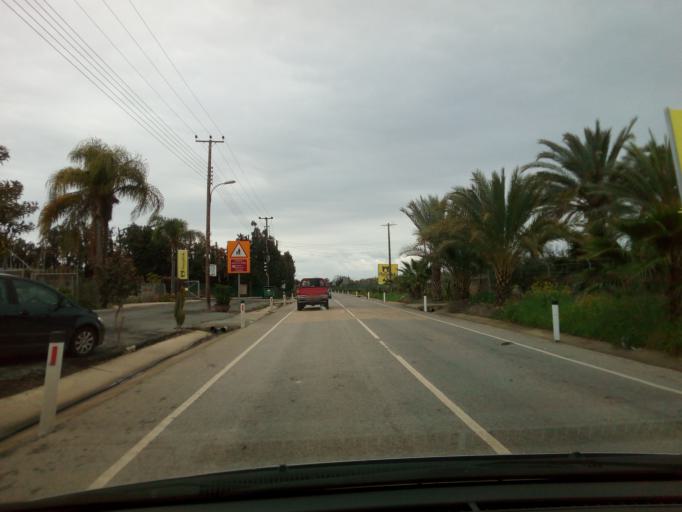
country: CY
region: Larnaka
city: Kofinou
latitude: 34.7420
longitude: 33.3267
